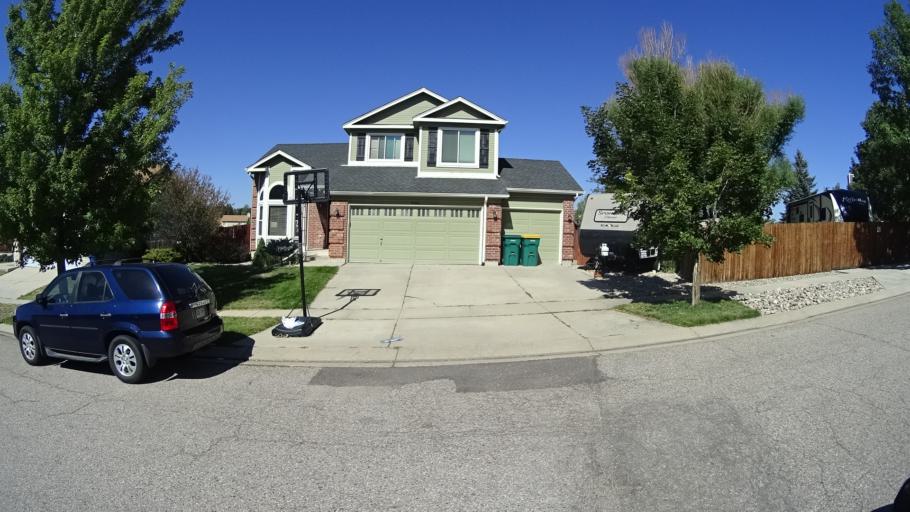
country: US
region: Colorado
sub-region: El Paso County
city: Black Forest
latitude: 38.9499
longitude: -104.7268
